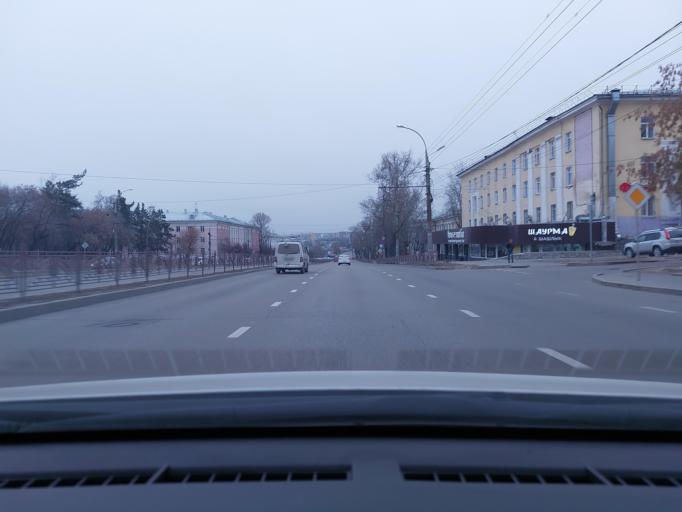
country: RU
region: Irkutsk
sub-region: Irkutskiy Rayon
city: Irkutsk
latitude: 52.2611
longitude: 104.2606
